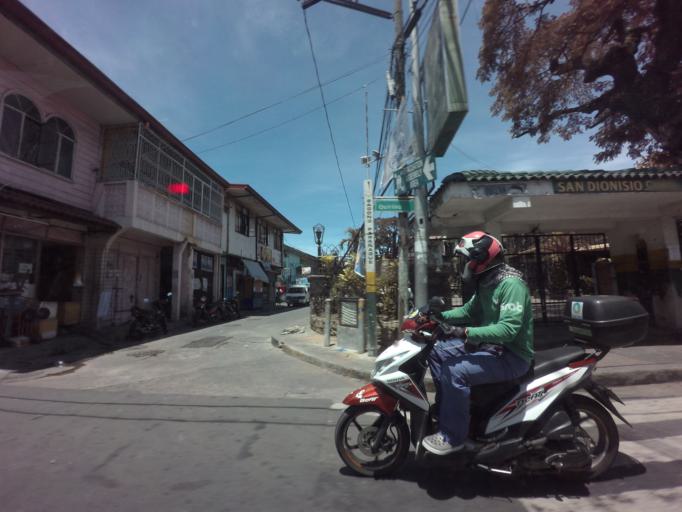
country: PH
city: Sambayanihan People's Village
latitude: 14.4959
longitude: 120.9894
